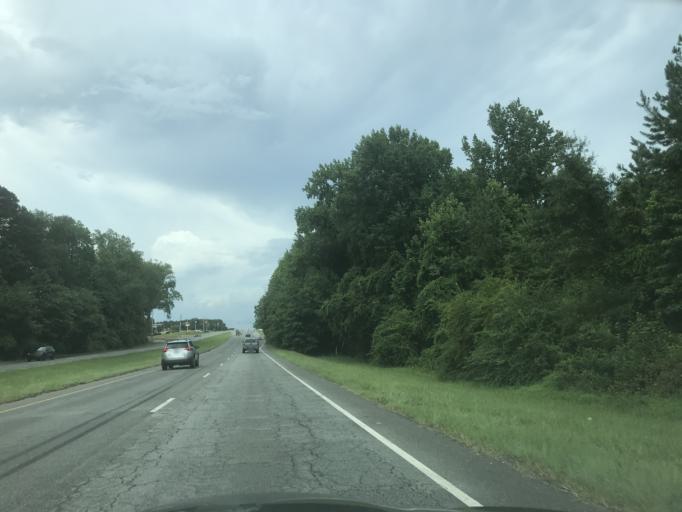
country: US
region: North Carolina
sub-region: Johnston County
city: Clayton
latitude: 35.6671
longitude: -78.5012
